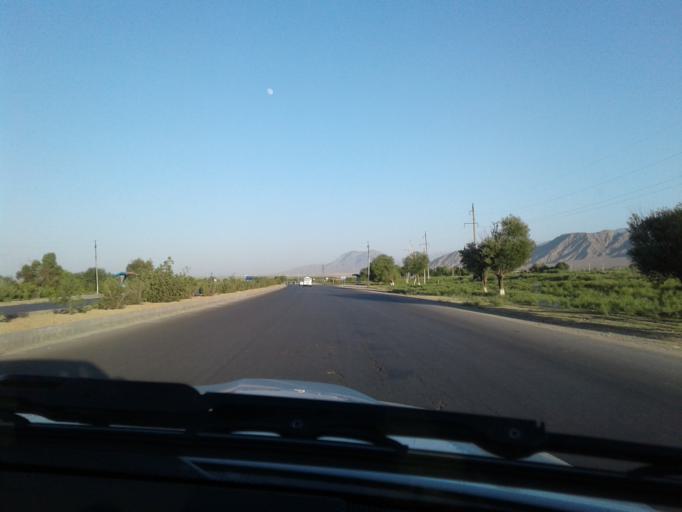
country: TM
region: Ahal
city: Arcabil
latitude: 38.1986
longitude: 57.8282
